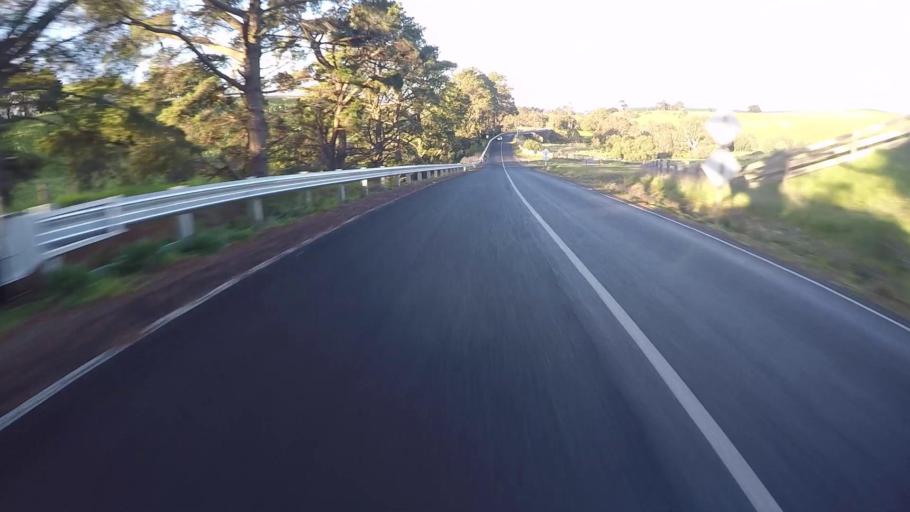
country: AU
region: Victoria
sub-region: Greater Geelong
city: Wandana Heights
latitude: -38.1455
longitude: 144.1842
